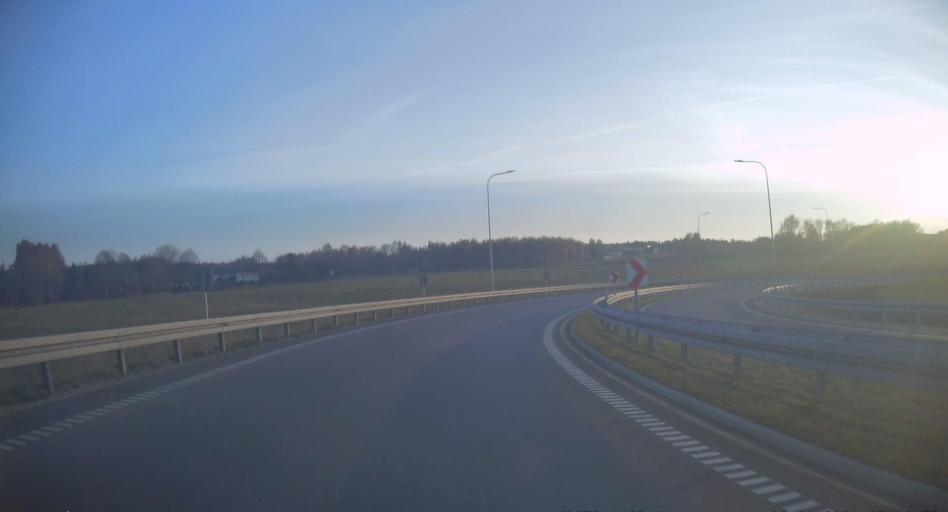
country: PL
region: Silesian Voivodeship
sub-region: Powiat klobucki
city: Kamyk
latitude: 50.8467
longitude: 19.0414
